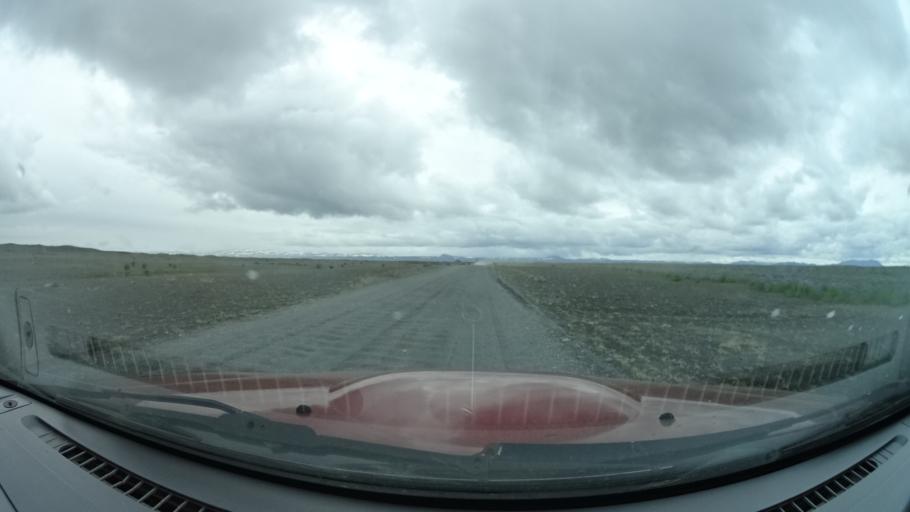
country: IS
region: Northeast
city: Laugar
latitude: 65.6983
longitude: -16.3100
